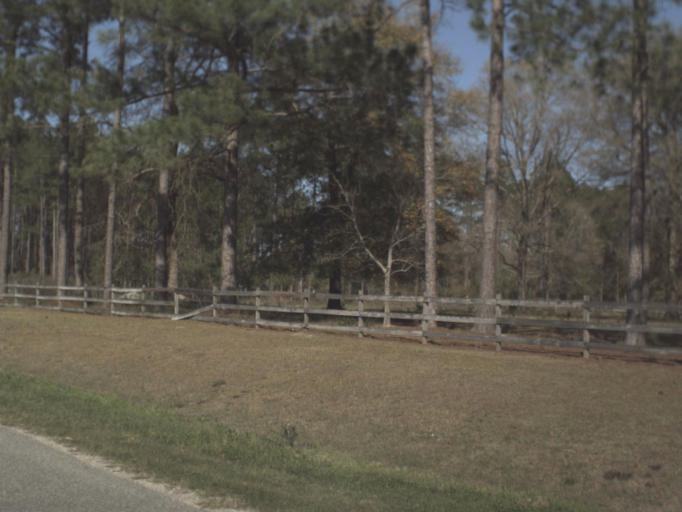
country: US
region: Florida
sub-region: Gulf County
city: Wewahitchka
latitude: 30.1719
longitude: -85.2058
